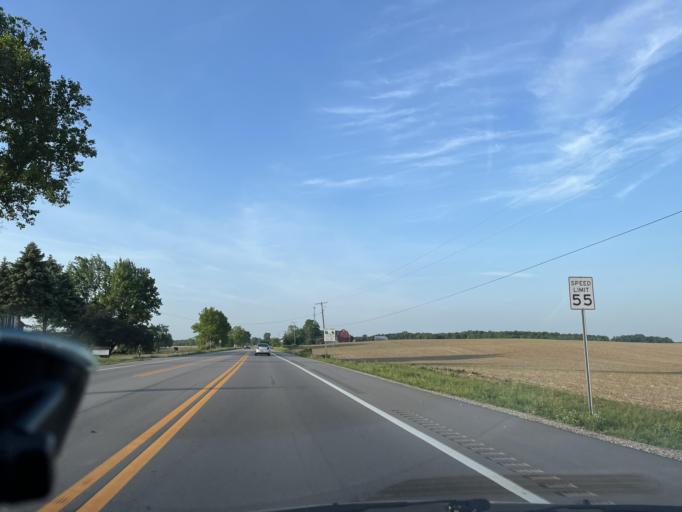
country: US
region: Michigan
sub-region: Kent County
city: Caledonia
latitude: 42.7678
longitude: -85.5065
